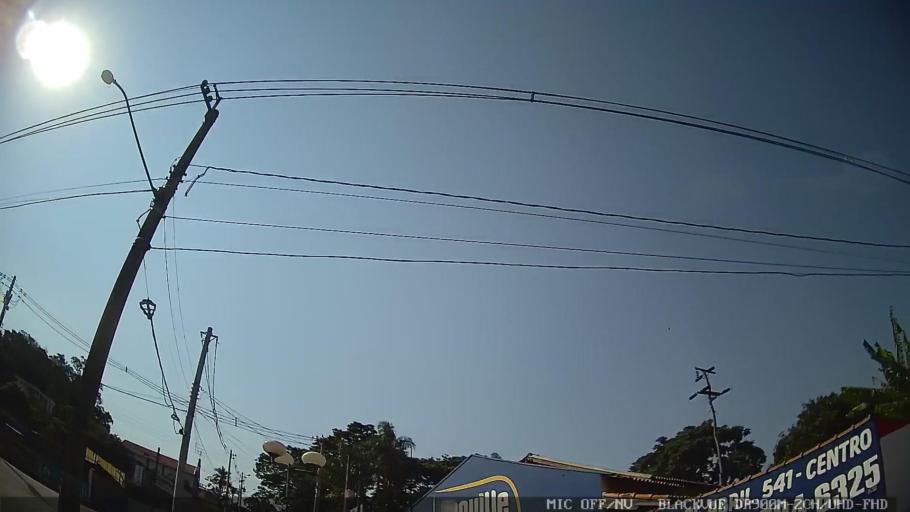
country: BR
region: Sao Paulo
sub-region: Itatiba
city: Itatiba
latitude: -22.9916
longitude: -46.8475
